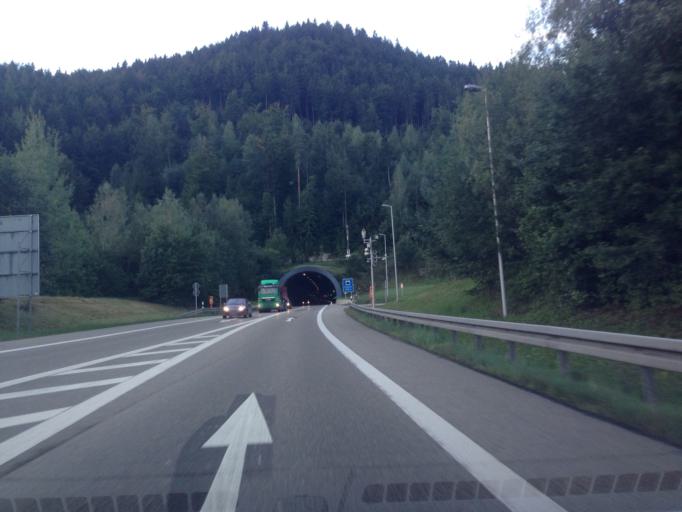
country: AT
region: Tyrol
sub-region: Politischer Bezirk Reutte
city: Vils
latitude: 47.5687
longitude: 10.6593
